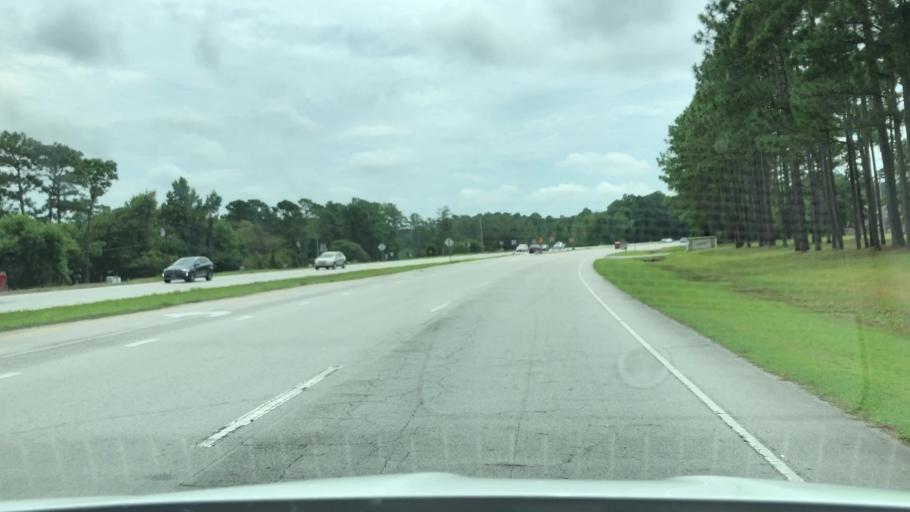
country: US
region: North Carolina
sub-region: Carteret County
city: Newport
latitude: 34.8269
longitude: -76.8767
